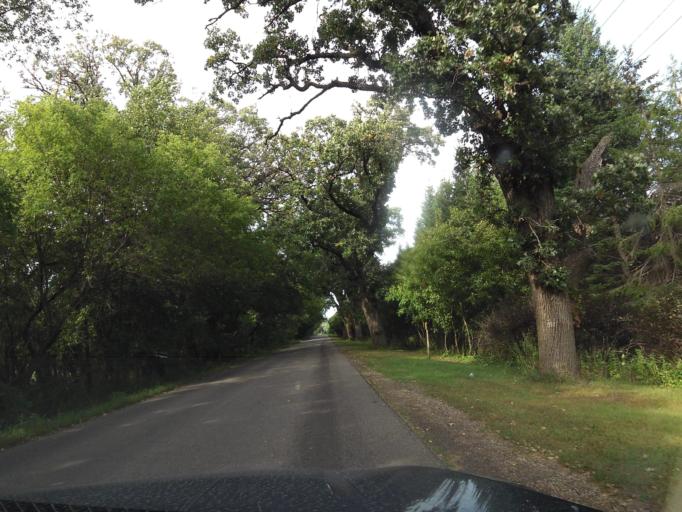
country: US
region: Minnesota
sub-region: Washington County
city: Afton
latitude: 44.8766
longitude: -92.8111
